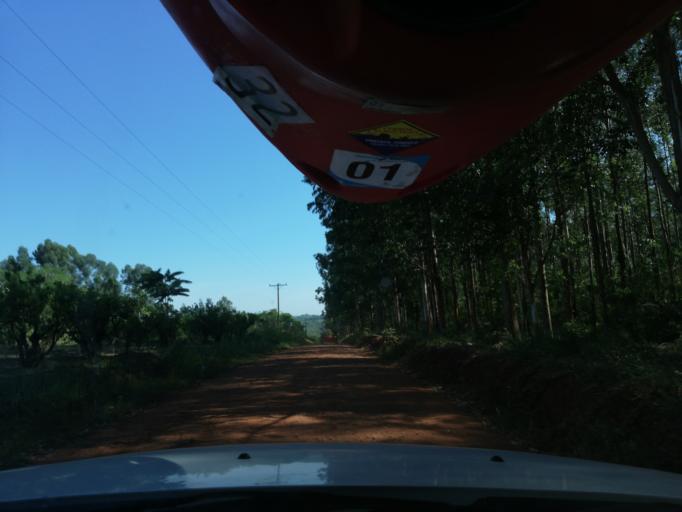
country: AR
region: Misiones
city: Puerto Leoni
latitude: -26.9666
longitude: -55.1526
